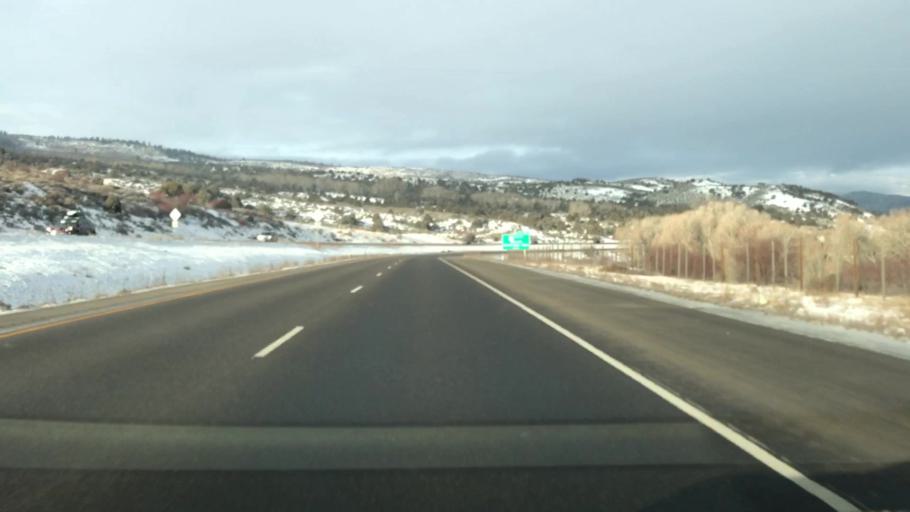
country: US
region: Colorado
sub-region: Eagle County
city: Edwards
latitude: 39.6827
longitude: -106.6550
